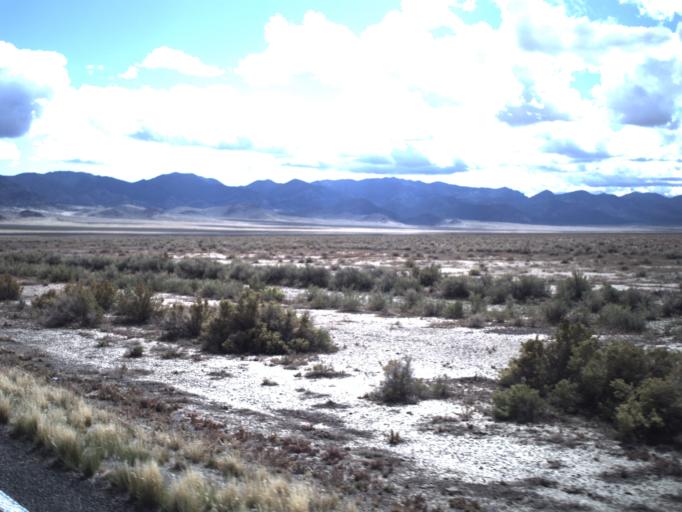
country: US
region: Utah
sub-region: Beaver County
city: Milford
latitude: 38.5288
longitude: -113.6723
